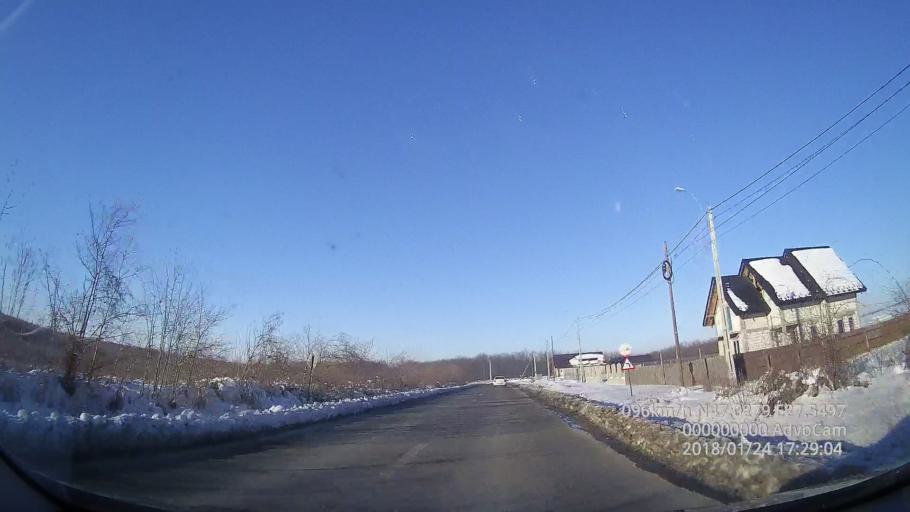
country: RO
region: Iasi
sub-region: Comuna Mogosesti
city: Mogosesti
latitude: 47.0287
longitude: 27.5497
